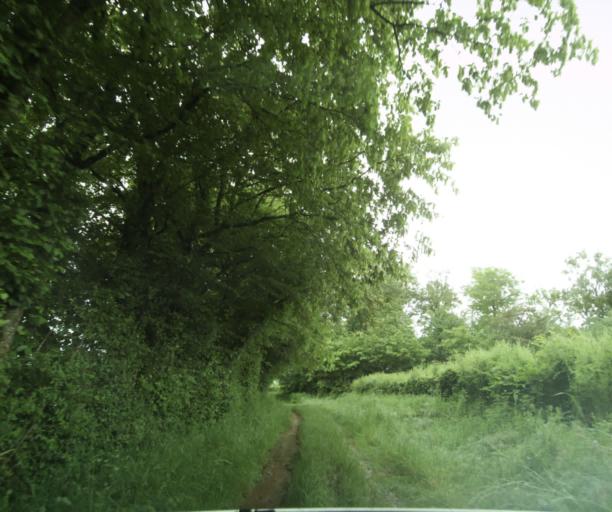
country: FR
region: Bourgogne
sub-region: Departement de Saone-et-Loire
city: Charolles
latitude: 46.4612
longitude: 4.3531
